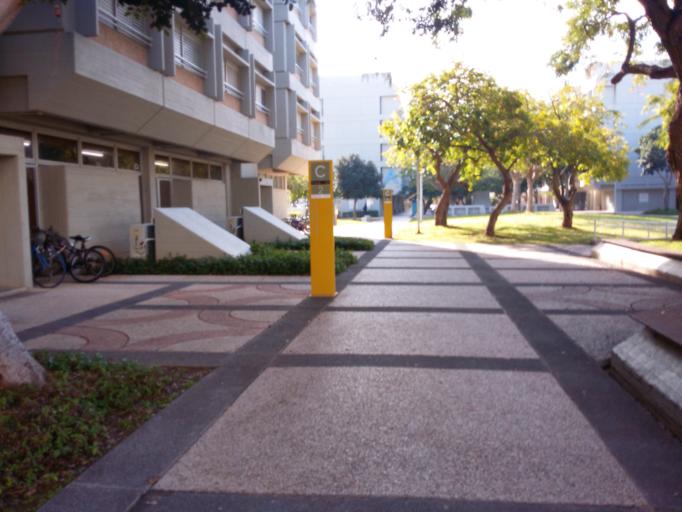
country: IL
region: Tel Aviv
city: Ramat Gan
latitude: 32.1129
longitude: 34.8013
